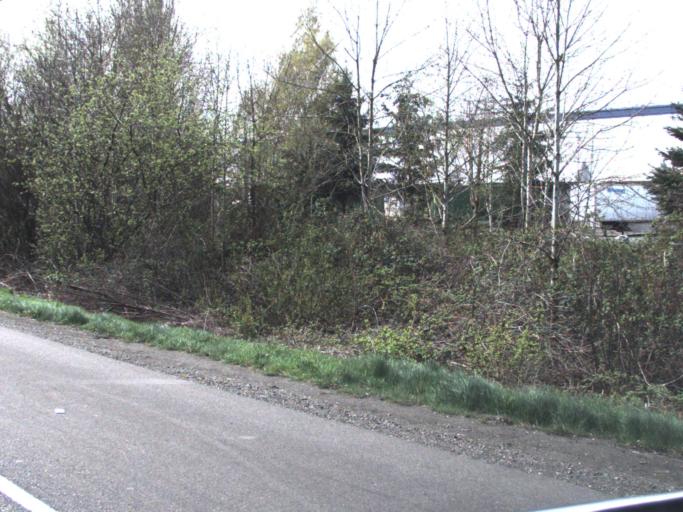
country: US
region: Washington
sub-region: King County
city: Kent
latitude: 47.4190
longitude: -122.2212
